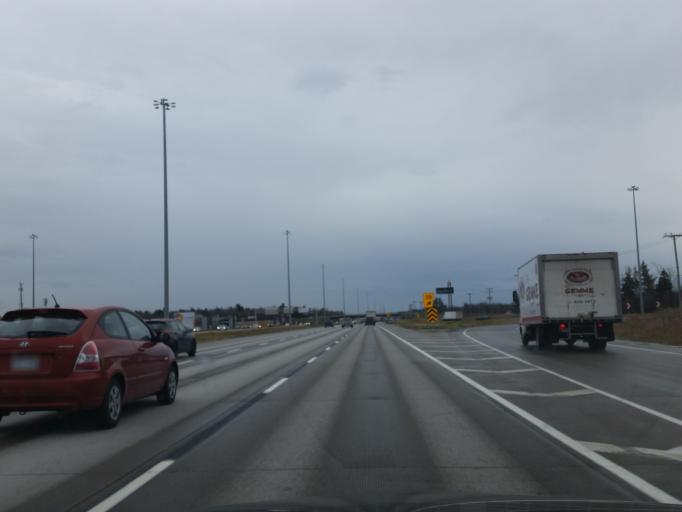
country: CA
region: Quebec
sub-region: Laurentides
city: Blainville
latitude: 45.6808
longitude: -73.9197
